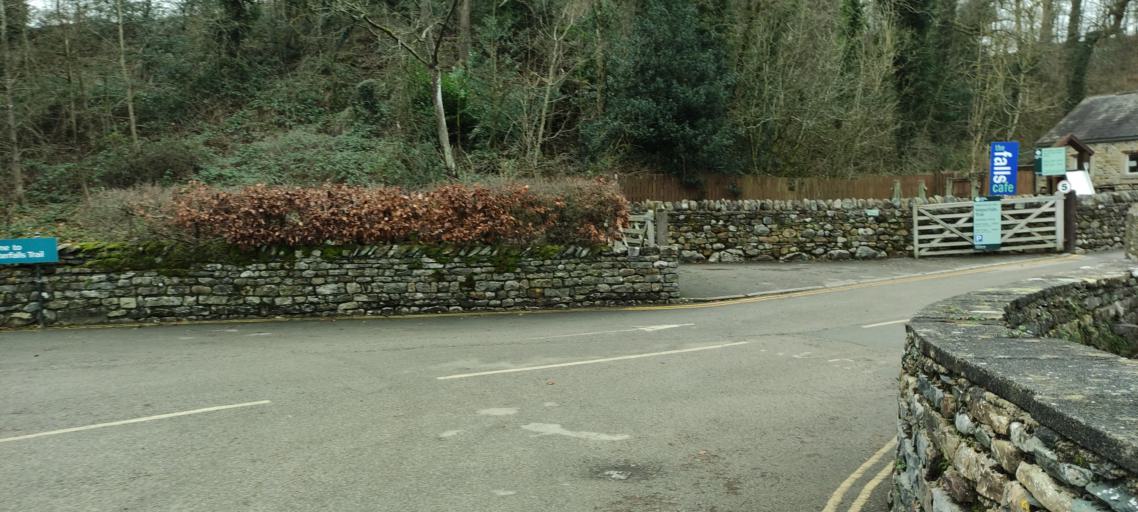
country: GB
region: England
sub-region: North Yorkshire
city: Ingleton
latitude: 54.1543
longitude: -2.4714
